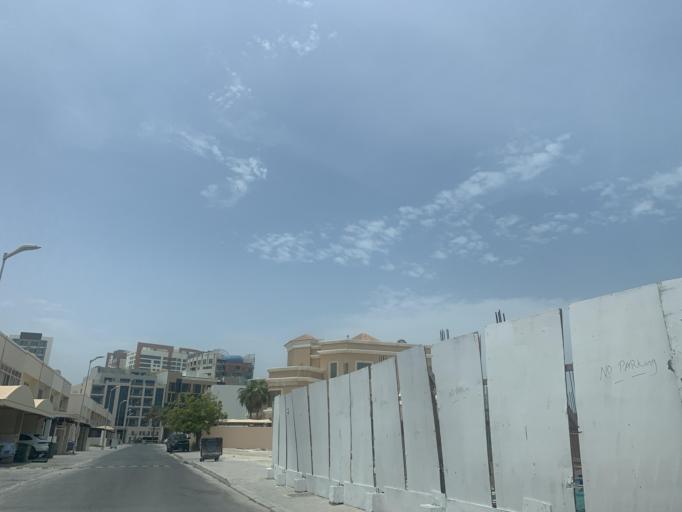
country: BH
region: Muharraq
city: Al Hadd
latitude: 26.2903
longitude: 50.6705
